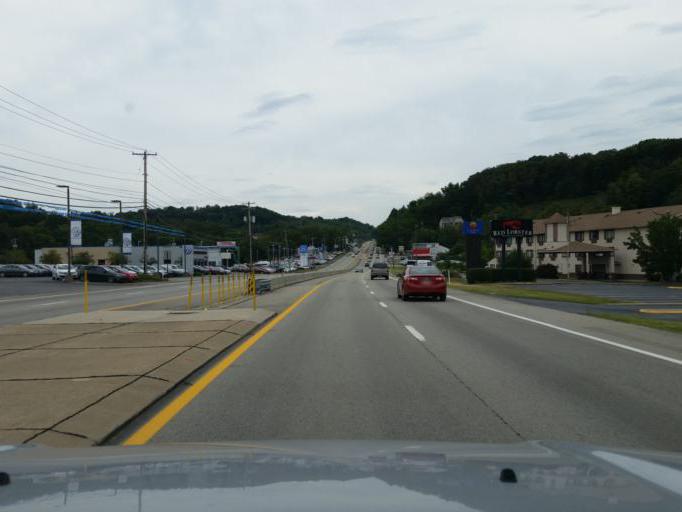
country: US
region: Pennsylvania
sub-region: Westmoreland County
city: Greensburg
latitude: 40.3012
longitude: -79.4918
